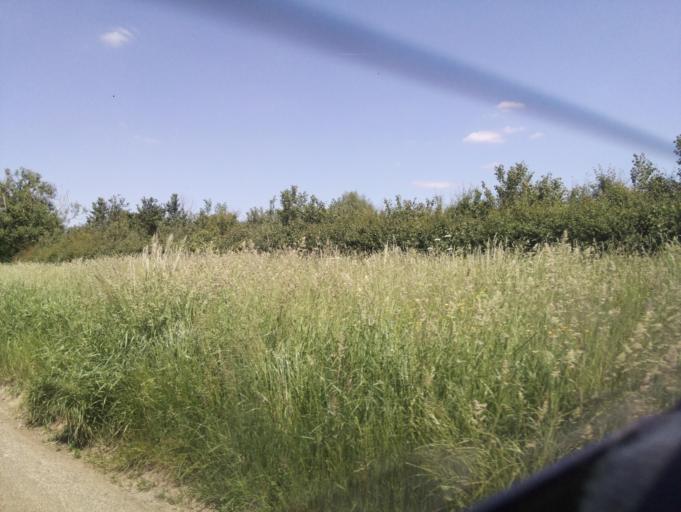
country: GB
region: England
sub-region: Wiltshire
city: Bremhill
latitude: 51.4876
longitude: -2.0432
